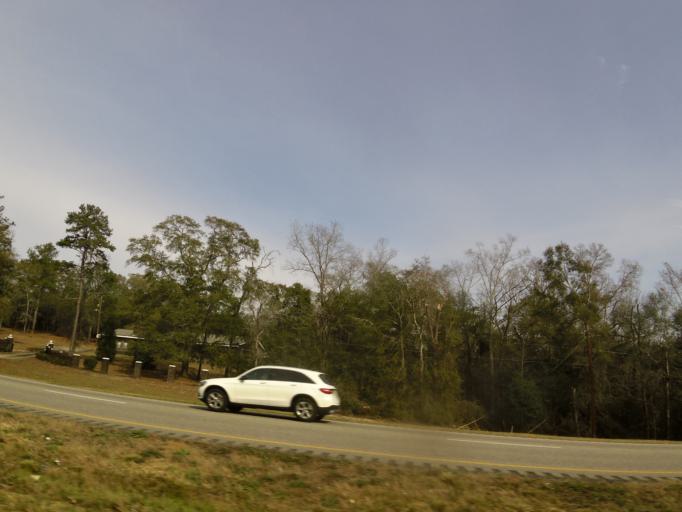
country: US
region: Alabama
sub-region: Dale County
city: Newton
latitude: 31.3980
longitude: -85.5897
